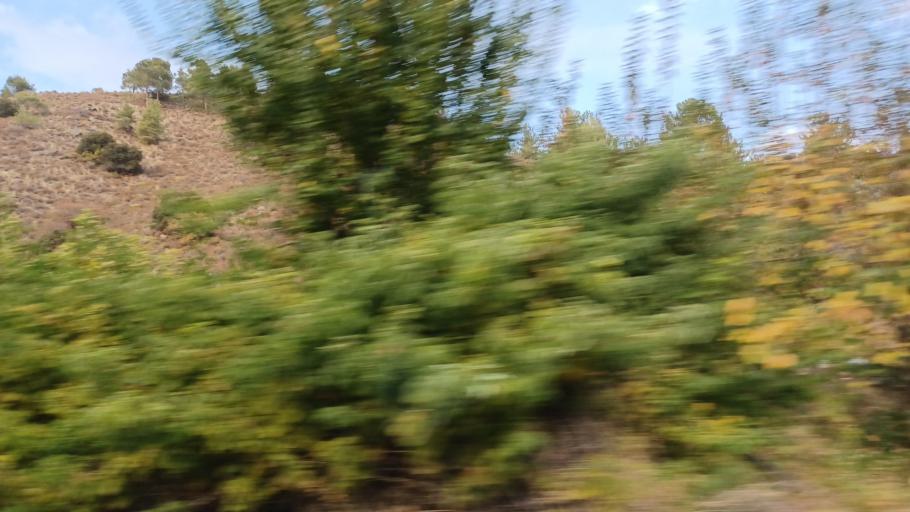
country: CY
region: Lefkosia
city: Kakopetria
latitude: 34.9774
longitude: 32.9099
